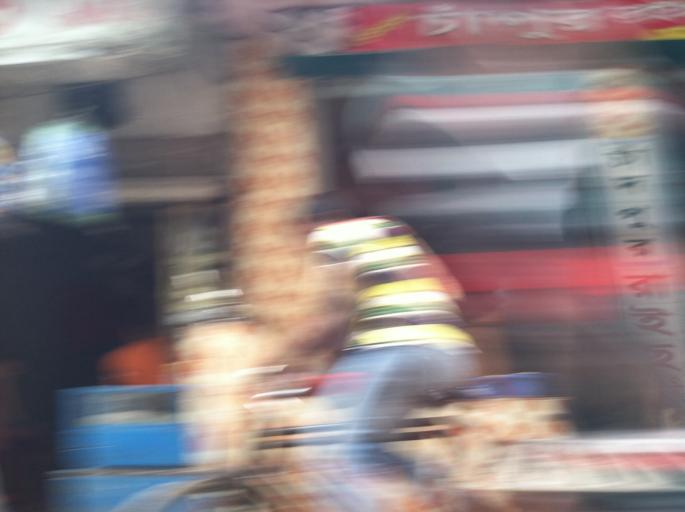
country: BD
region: Dhaka
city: Paltan
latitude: 23.7295
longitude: 90.4292
